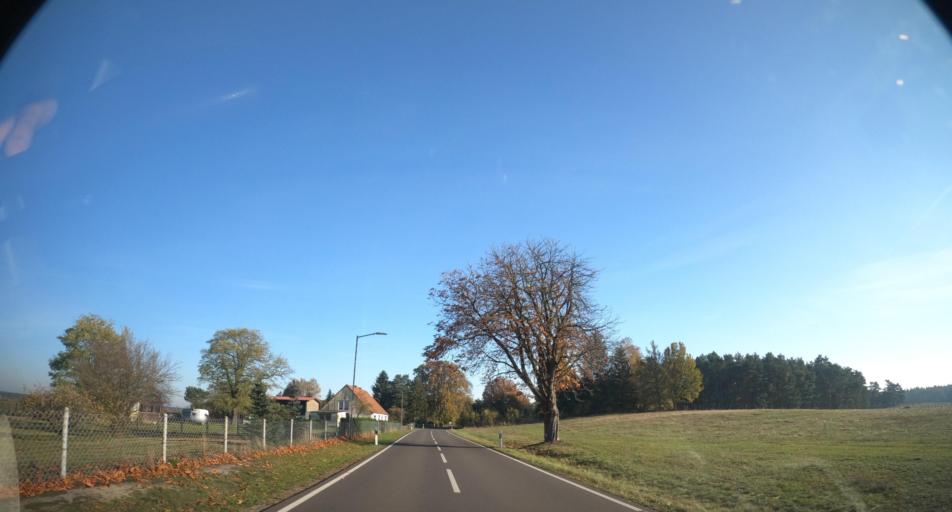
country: DE
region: Mecklenburg-Vorpommern
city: Ahlbeck
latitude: 53.6441
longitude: 14.2007
